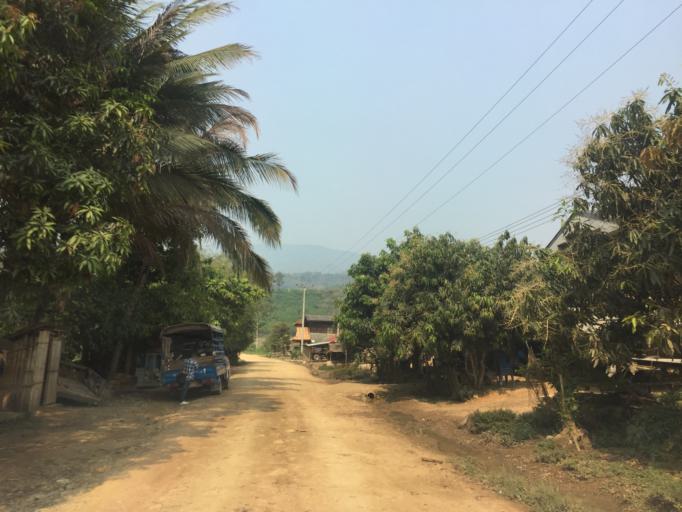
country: TH
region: Phayao
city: Phu Sang
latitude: 19.6045
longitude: 100.5372
